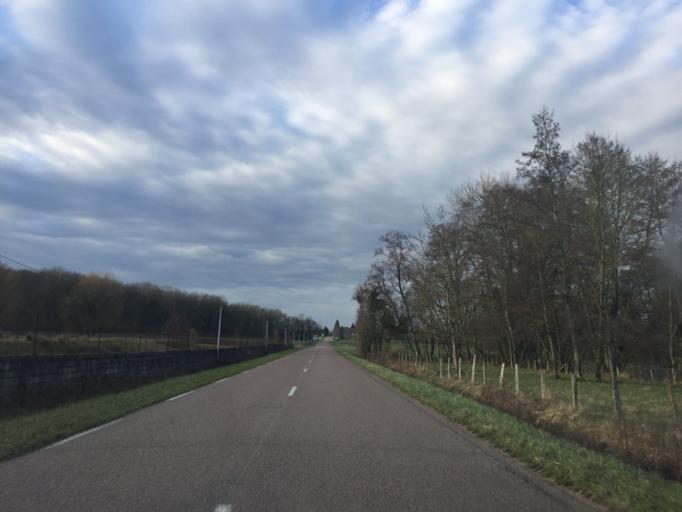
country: FR
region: Franche-Comte
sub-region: Departement du Jura
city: Arbois
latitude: 46.9281
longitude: 5.6859
